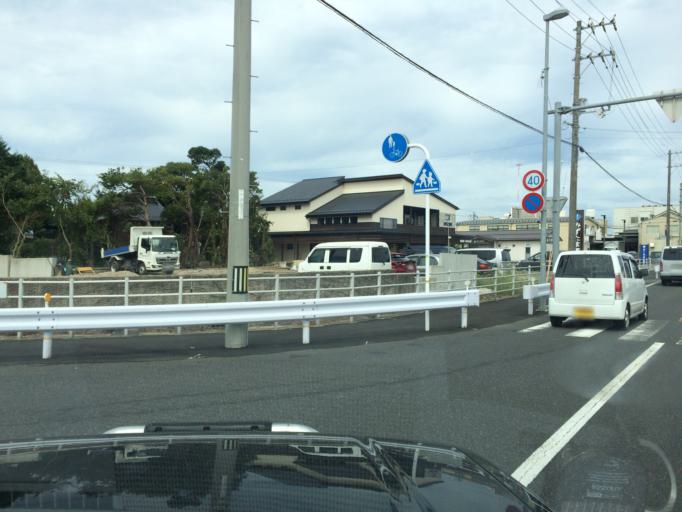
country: JP
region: Tottori
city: Tottori
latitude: 35.5016
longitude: 134.1934
